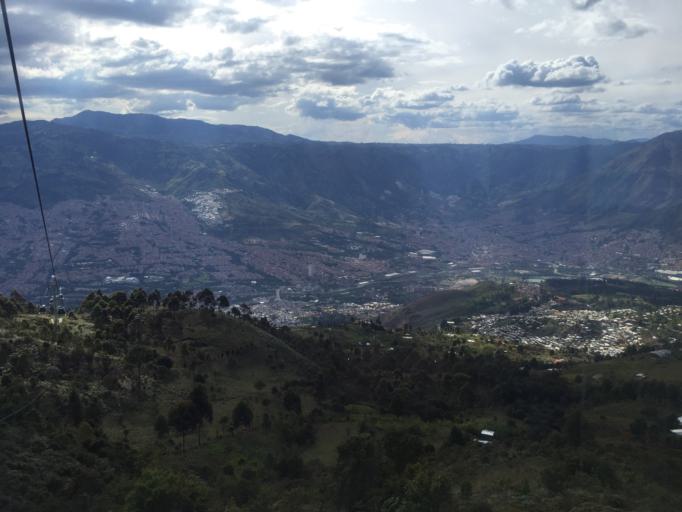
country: CO
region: Antioquia
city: Medellin
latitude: 6.2884
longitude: -75.5264
